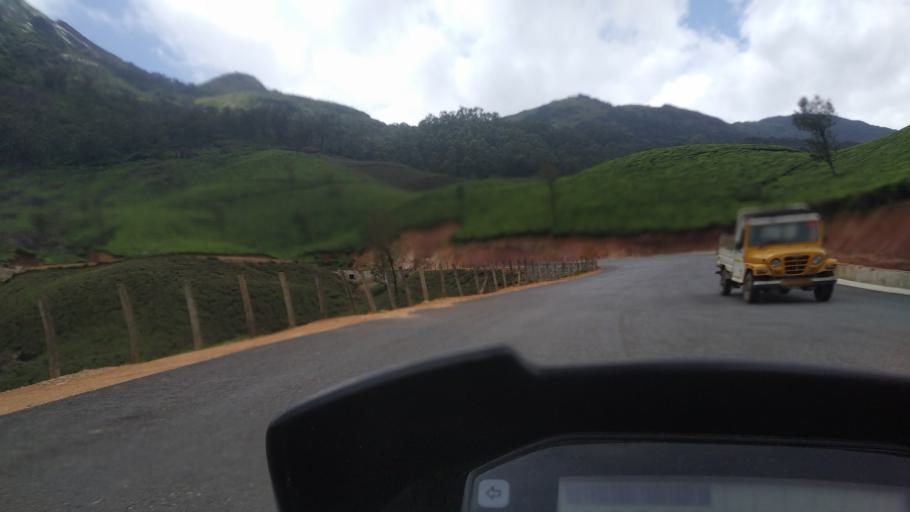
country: IN
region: Kerala
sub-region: Idukki
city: Munnar
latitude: 10.0454
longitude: 77.1124
